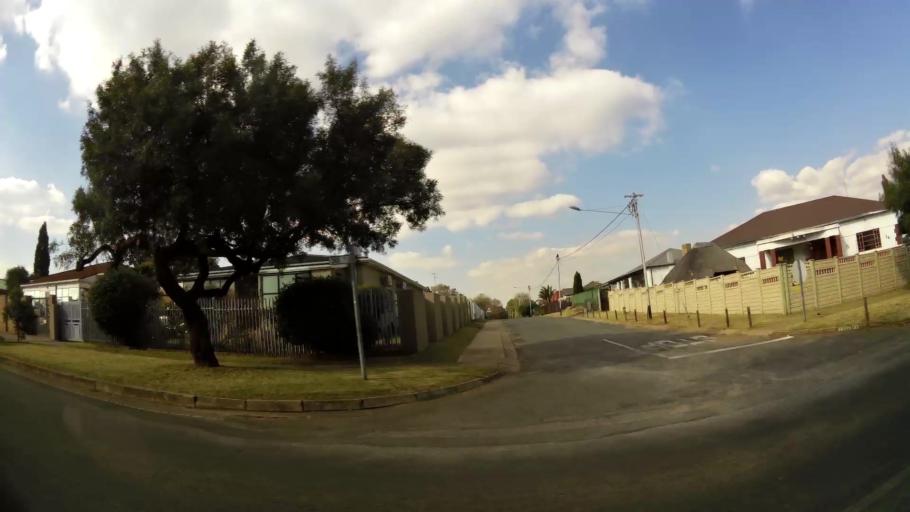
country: ZA
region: Gauteng
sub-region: West Rand District Municipality
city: Krugersdorp
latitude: -26.0902
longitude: 27.7710
